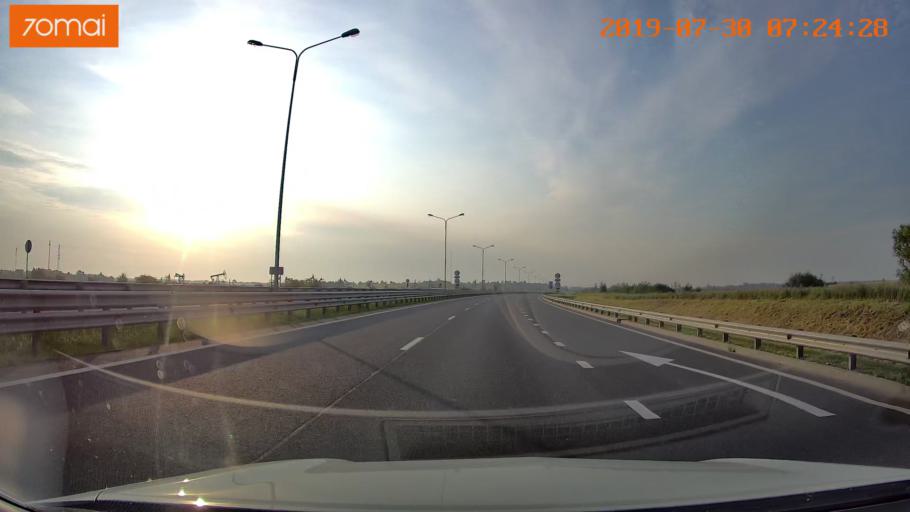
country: RU
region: Kaliningrad
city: Bol'shoe Isakovo
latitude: 54.6930
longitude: 20.8131
